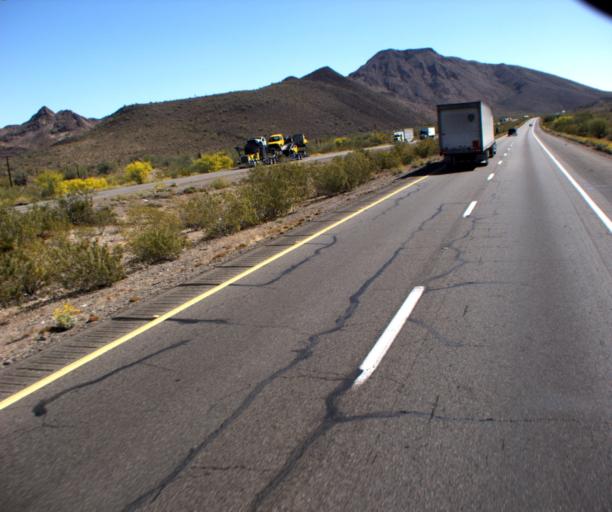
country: US
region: Arizona
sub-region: La Paz County
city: Quartzsite
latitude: 33.6787
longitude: -114.0738
